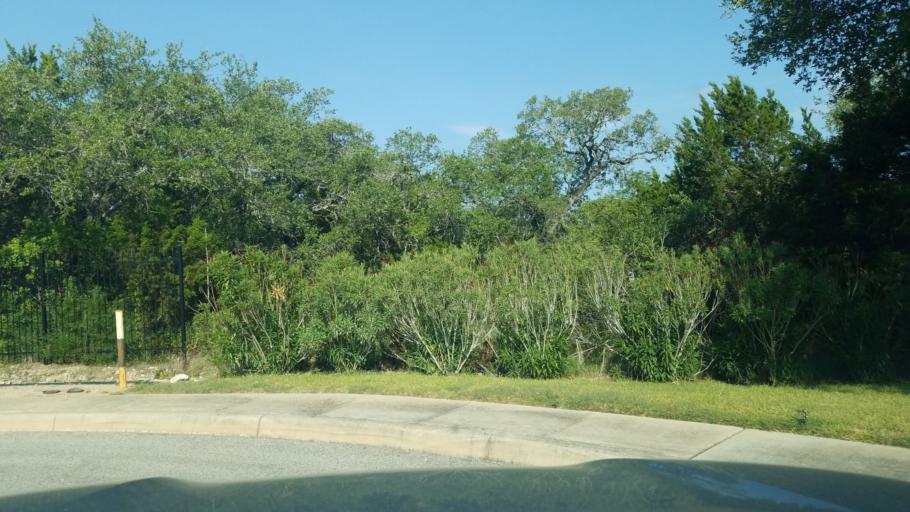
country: US
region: Texas
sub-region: Medina County
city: La Coste
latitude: 29.4419
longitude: -98.7538
